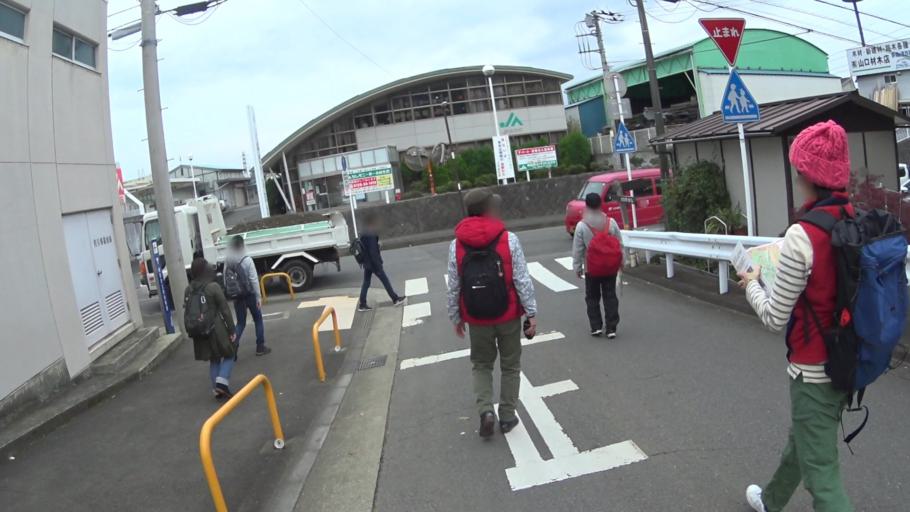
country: JP
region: Kanagawa
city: Hadano
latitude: 35.3952
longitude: 139.2318
